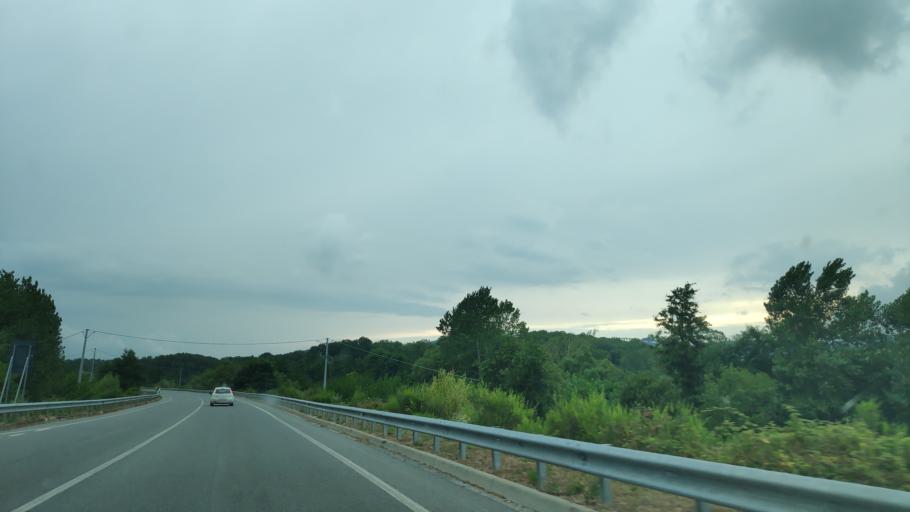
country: IT
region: Calabria
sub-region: Provincia di Catanzaro
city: Cardinale
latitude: 38.6632
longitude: 16.3913
